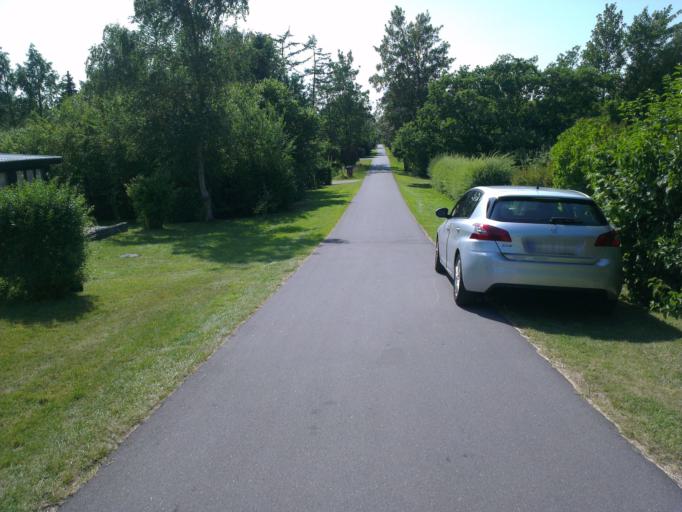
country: DK
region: Capital Region
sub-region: Halsnaes Kommune
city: Hundested
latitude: 55.9192
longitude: 11.9138
